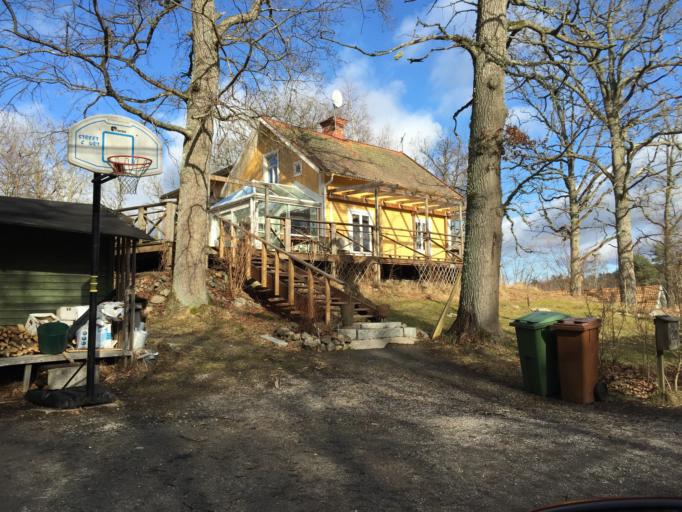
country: SE
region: Stockholm
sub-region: Salems Kommun
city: Ronninge
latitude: 59.1861
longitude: 17.7180
